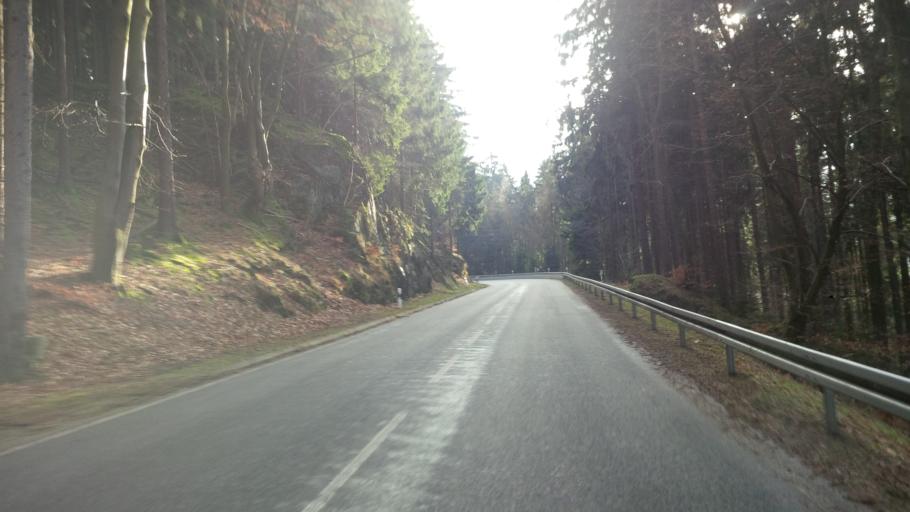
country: DE
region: Hesse
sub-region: Regierungsbezirk Darmstadt
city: Schmitten
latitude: 50.2563
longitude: 8.4731
